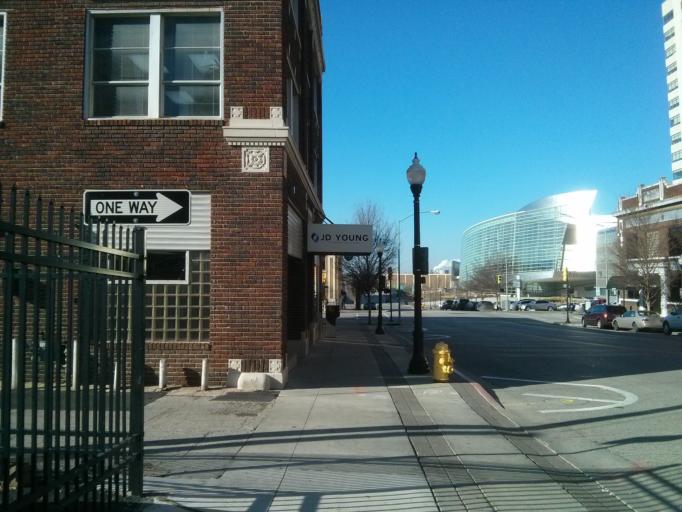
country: US
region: Oklahoma
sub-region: Tulsa County
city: Tulsa
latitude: 36.1529
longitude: -95.9930
